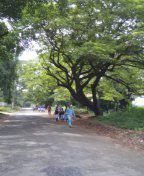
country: IN
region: Kerala
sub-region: Thrissur District
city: Trichur
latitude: 10.5283
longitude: 76.3640
